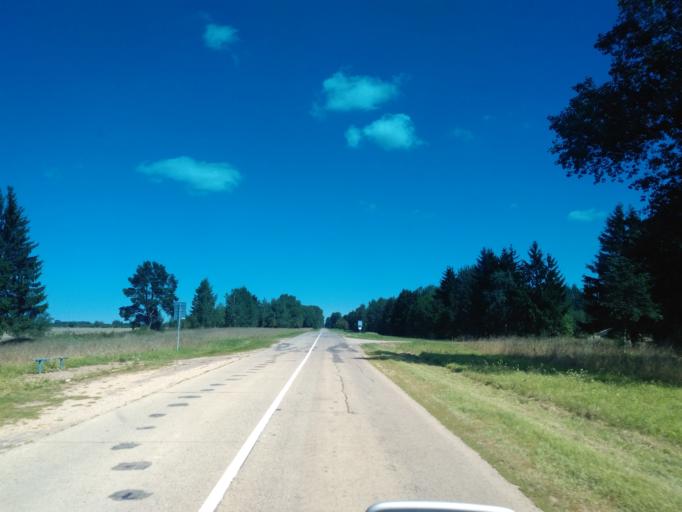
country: BY
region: Minsk
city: Stan'kava
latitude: 53.6482
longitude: 27.3029
